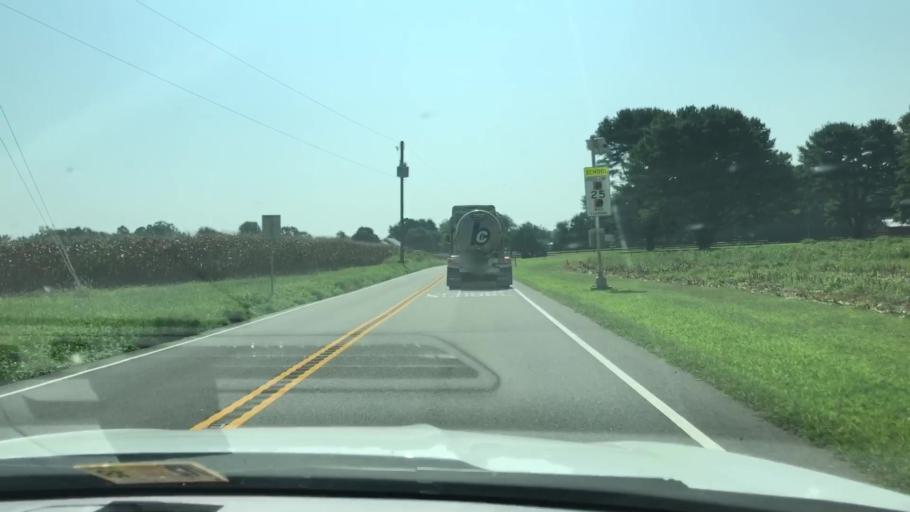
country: US
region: Virginia
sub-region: King William County
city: West Point
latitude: 37.6148
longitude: -76.7864
